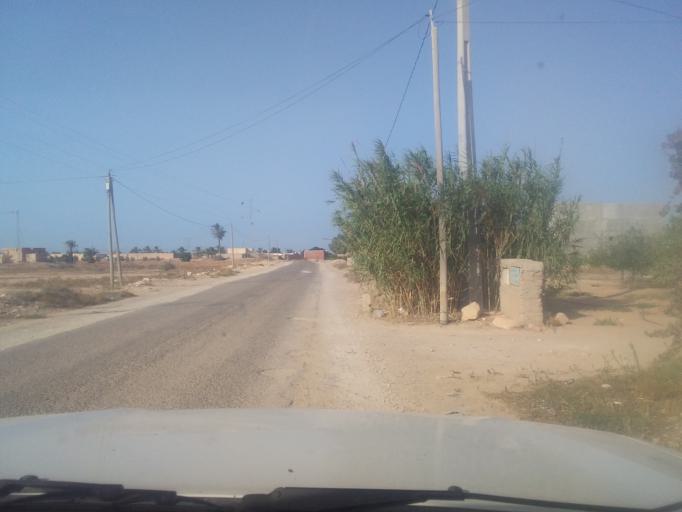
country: TN
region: Qabis
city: Matmata
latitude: 33.5899
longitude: 10.2786
